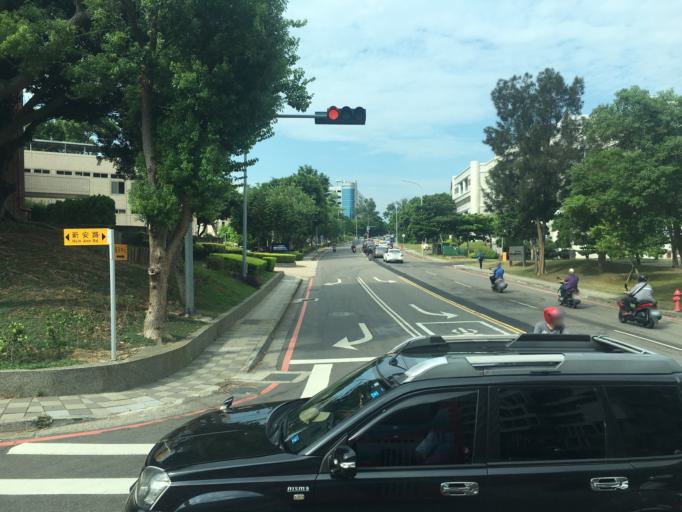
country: TW
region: Taiwan
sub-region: Hsinchu
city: Hsinchu
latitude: 24.7832
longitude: 120.9965
